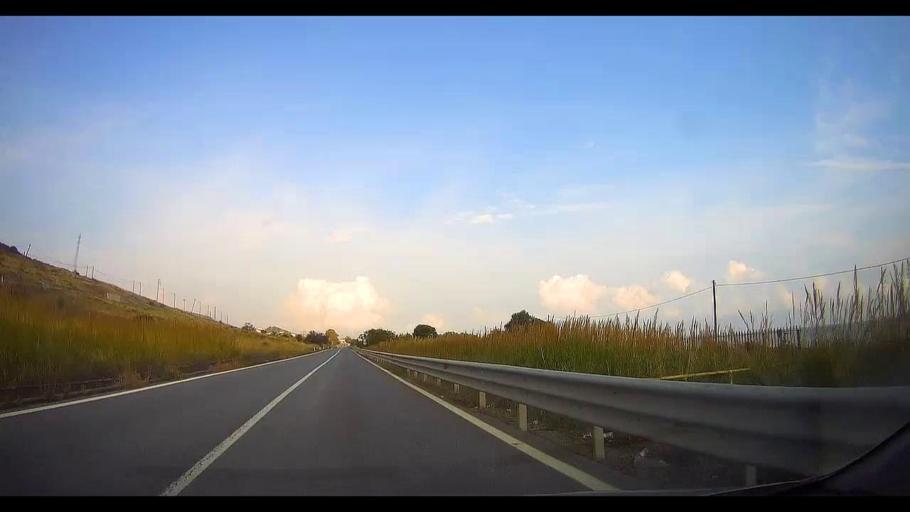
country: IT
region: Calabria
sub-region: Provincia di Cosenza
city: Cariati
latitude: 39.5187
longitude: 16.9074
